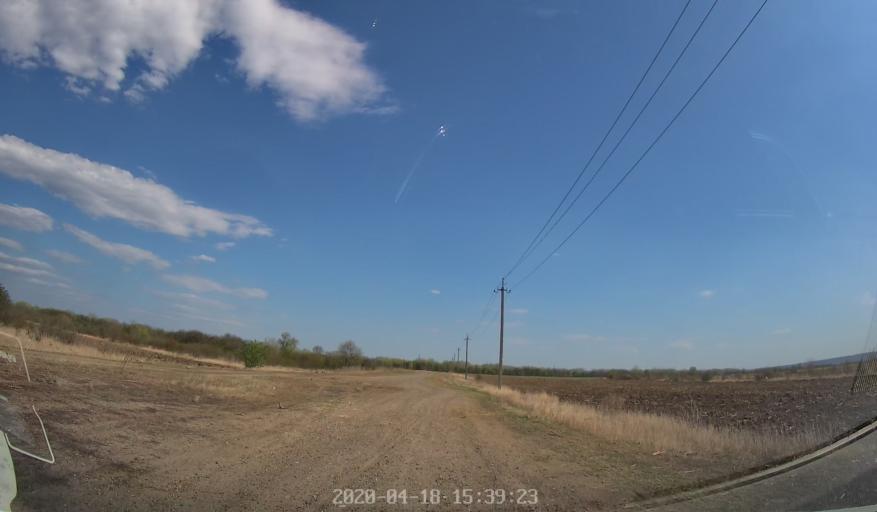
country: MD
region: Chisinau
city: Vadul lui Voda
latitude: 47.1465
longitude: 29.0886
